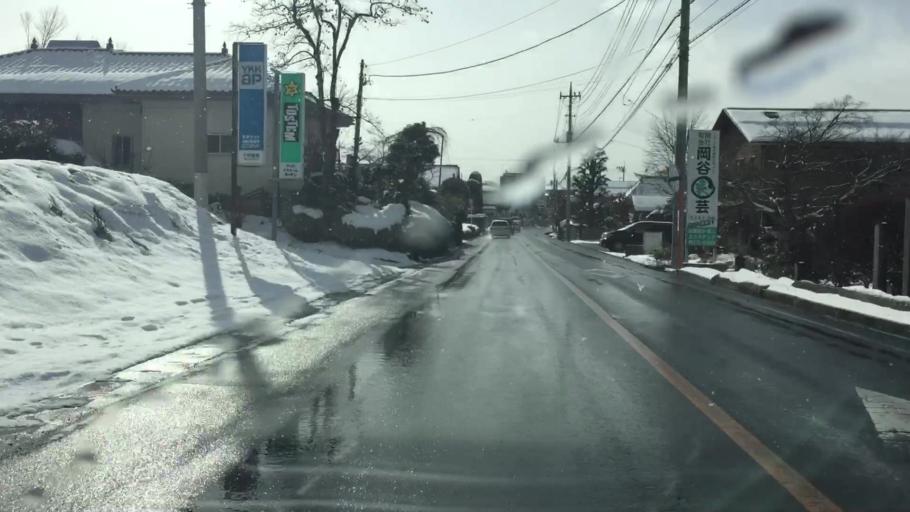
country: JP
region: Gunma
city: Numata
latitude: 36.6708
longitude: 139.0627
